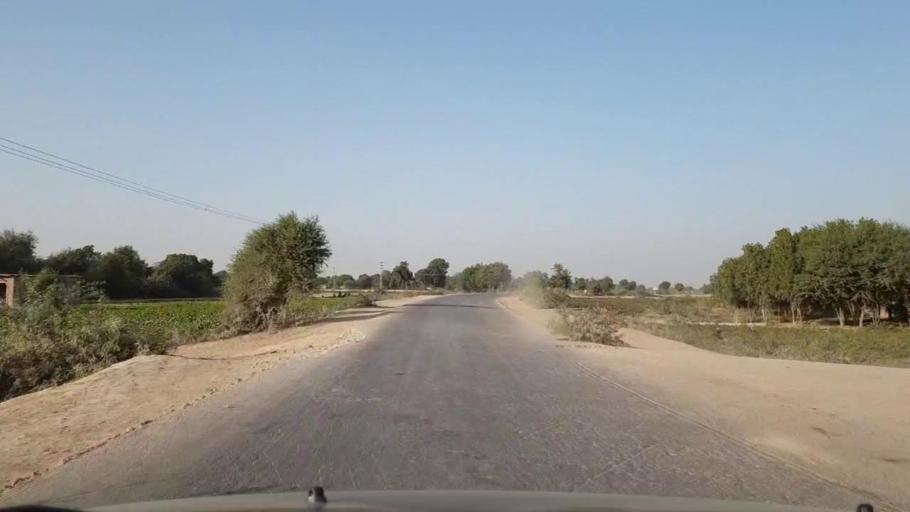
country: PK
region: Sindh
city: Chambar
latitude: 25.2296
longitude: 68.7829
